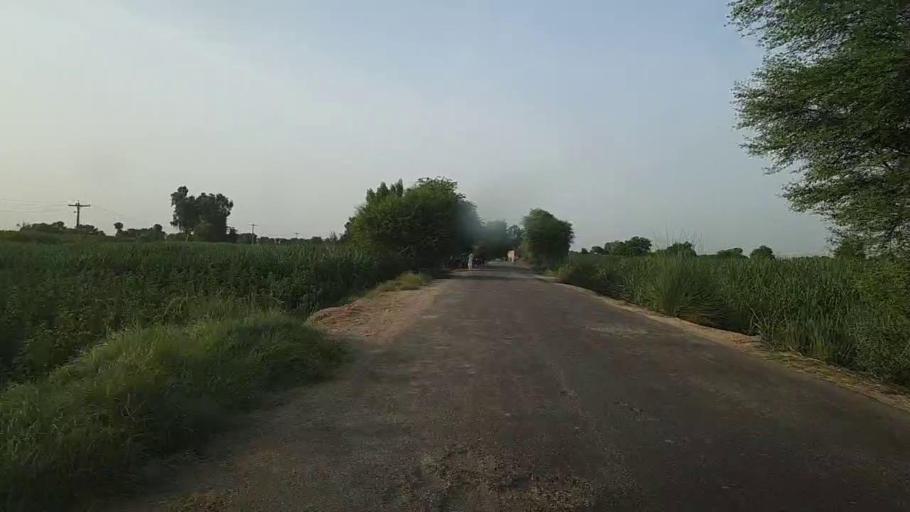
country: PK
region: Sindh
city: Ubauro
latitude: 28.1753
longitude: 69.8291
